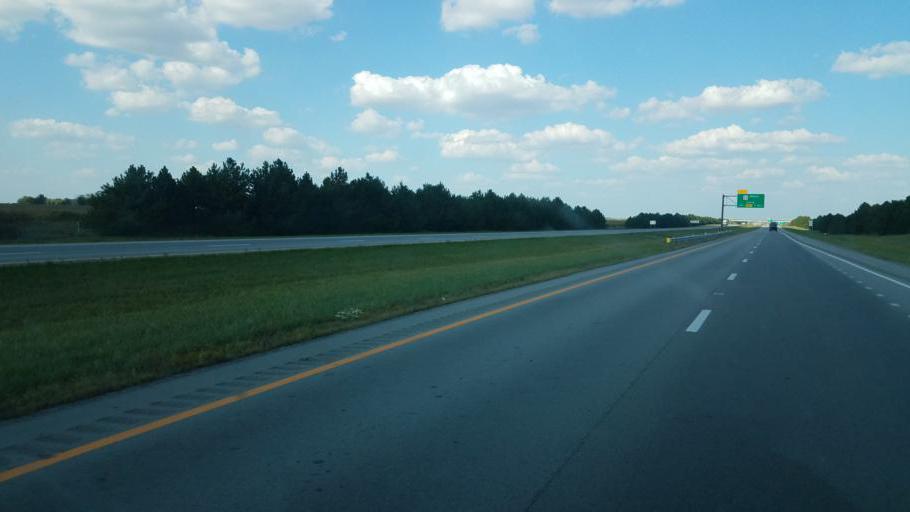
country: US
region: Ohio
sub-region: Wyandot County
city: Upper Sandusky
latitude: 40.8386
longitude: -83.3315
